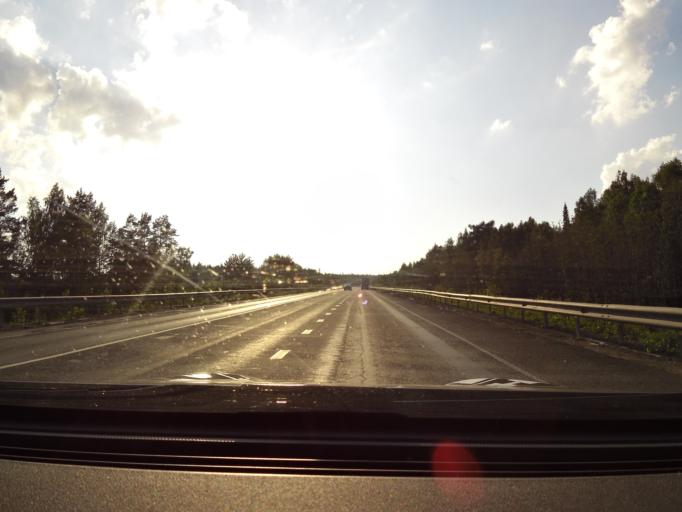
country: RU
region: Sverdlovsk
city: Revda
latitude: 56.8287
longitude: 59.8582
